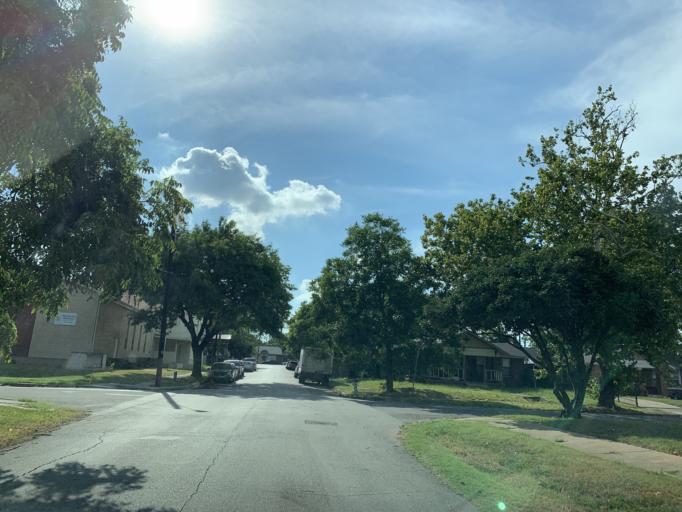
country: US
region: Texas
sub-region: Dallas County
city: Cockrell Hill
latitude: 32.7334
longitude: -96.8552
